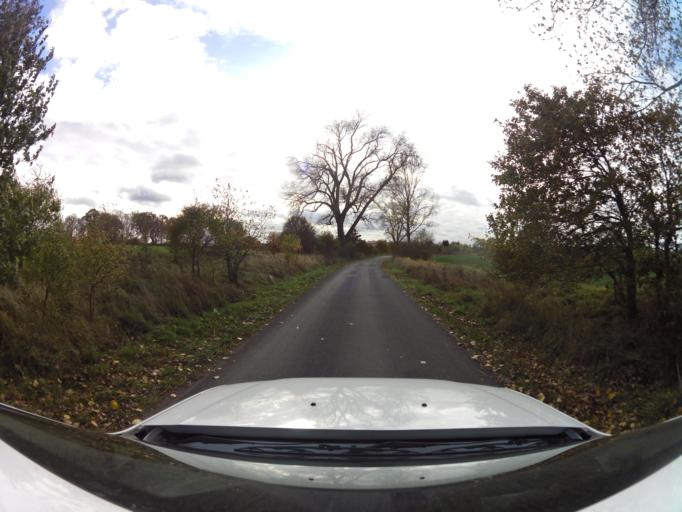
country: PL
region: West Pomeranian Voivodeship
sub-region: Powiat gryficki
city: Gryfice
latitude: 53.8939
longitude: 15.1271
